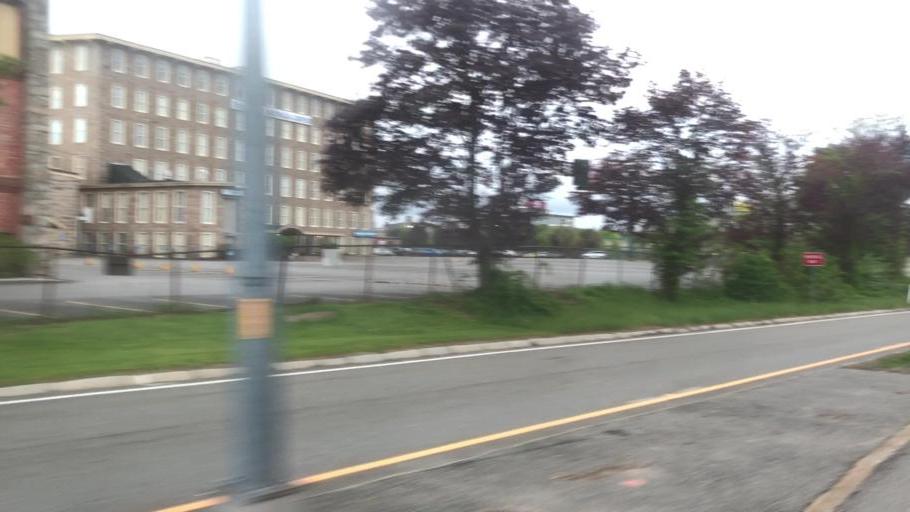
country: US
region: Massachusetts
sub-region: Bristol County
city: Fall River
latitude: 41.6997
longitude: -71.1514
